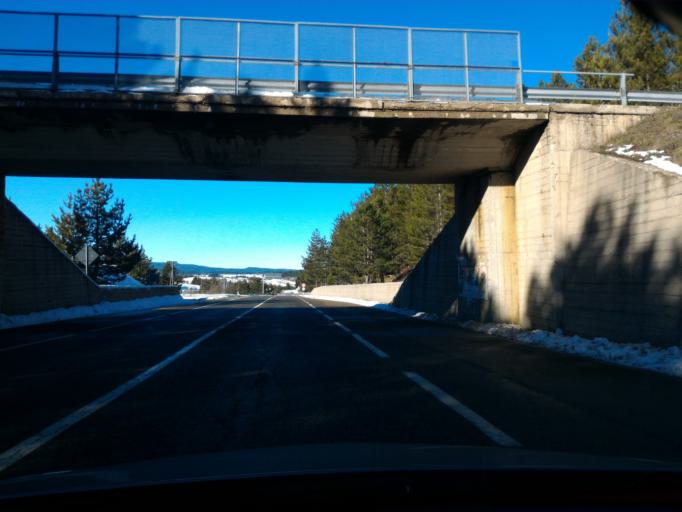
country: IT
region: Calabria
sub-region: Provincia di Cosenza
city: Longobucco
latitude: 39.3164
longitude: 16.5465
